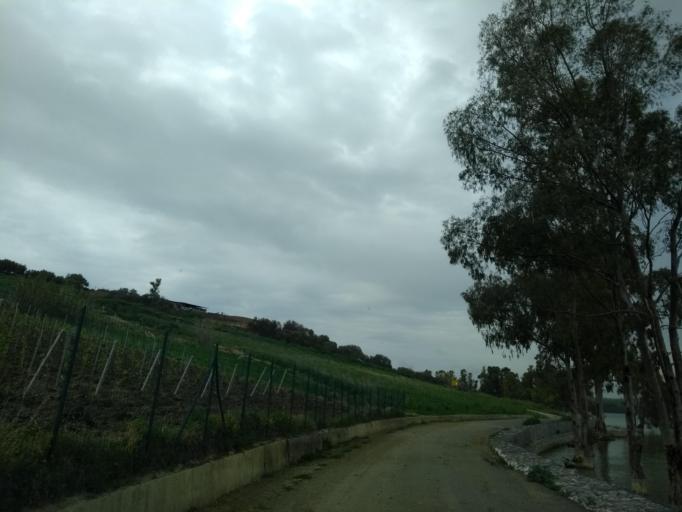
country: IT
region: Sicily
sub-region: Palermo
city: Partinico
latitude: 37.9940
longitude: 13.0822
